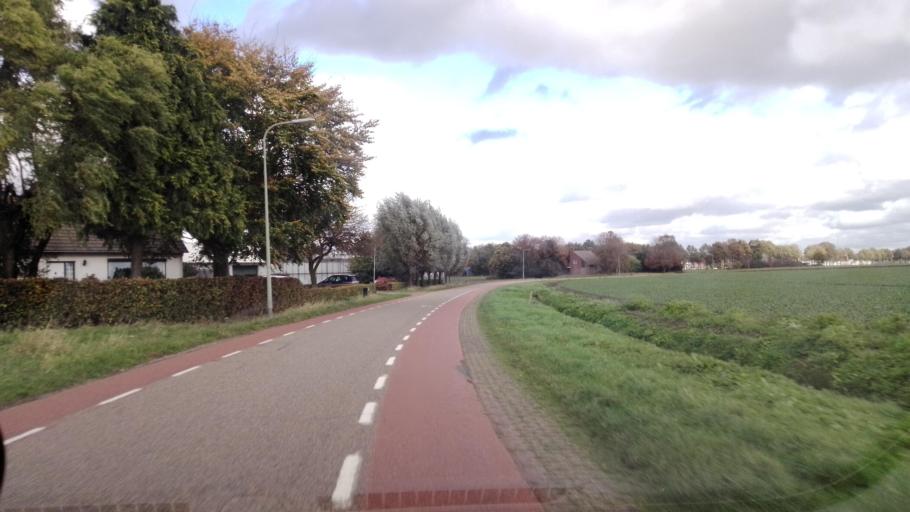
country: NL
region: Limburg
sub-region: Gemeente Venray
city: Venray
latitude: 51.5103
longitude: 5.9564
